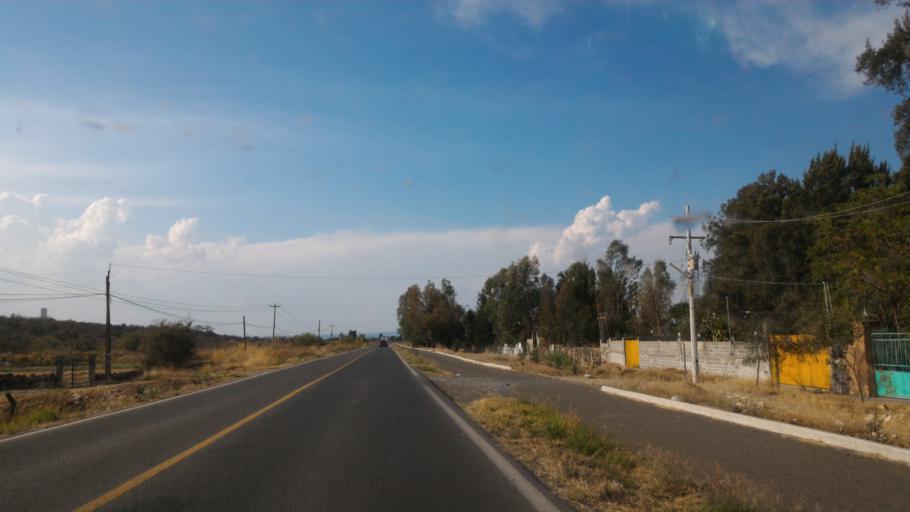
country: MX
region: Guanajuato
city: Ciudad Manuel Doblado
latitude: 20.7479
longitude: -101.9606
